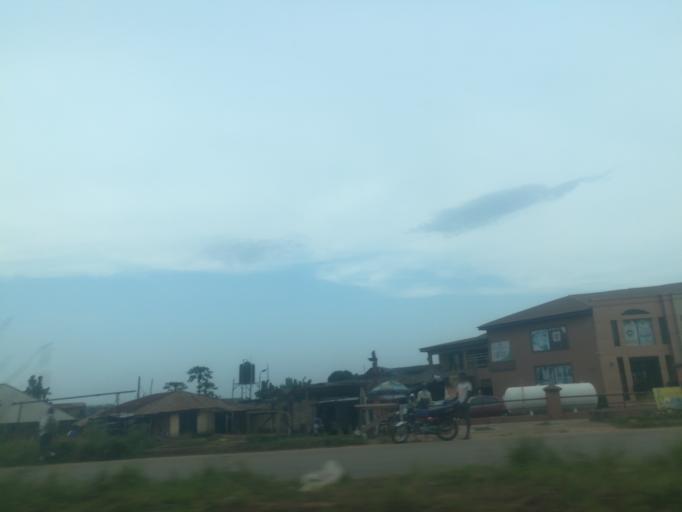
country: NG
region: Oyo
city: Ibadan
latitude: 7.3664
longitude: 3.8128
